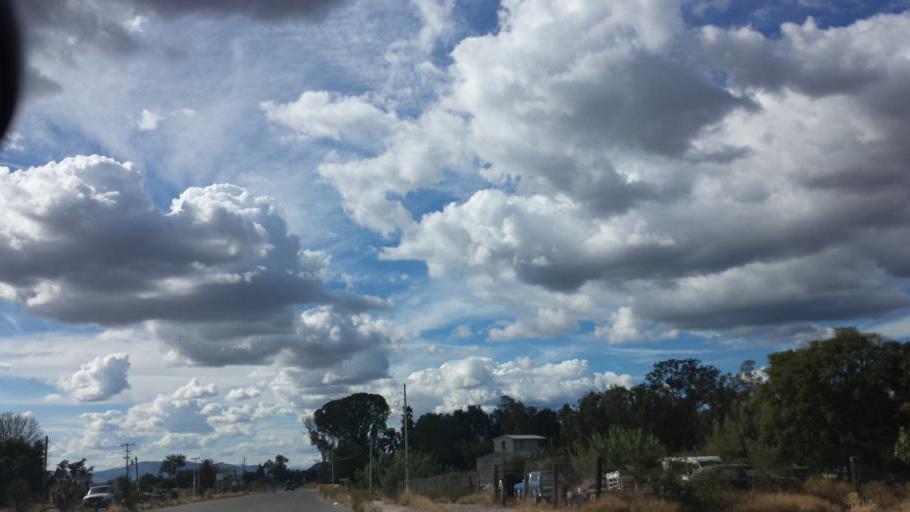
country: MX
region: Oaxaca
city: Tlacolula de Matamoros
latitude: 16.9503
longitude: -96.4641
